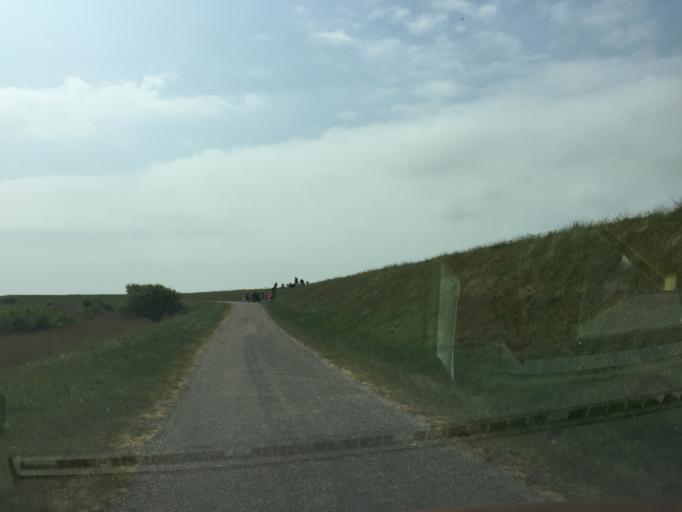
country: DK
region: South Denmark
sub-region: Esbjerg Kommune
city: Tjaereborg
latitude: 55.2905
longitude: 8.5473
